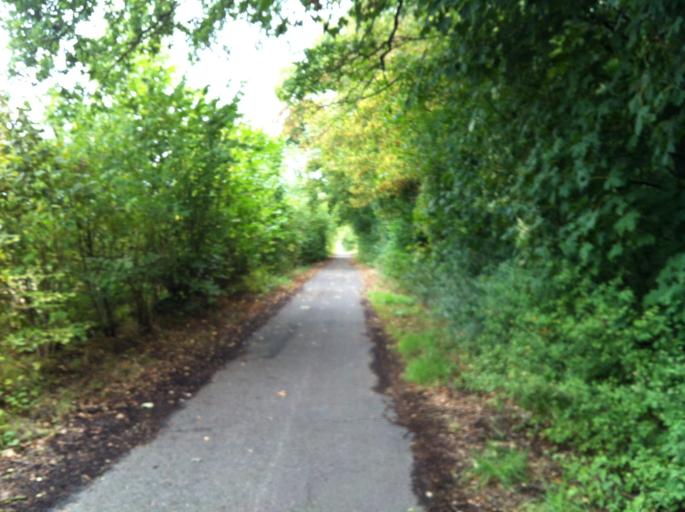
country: DE
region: Rheinland-Pfalz
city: Essenheim
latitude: 49.9603
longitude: 8.1562
